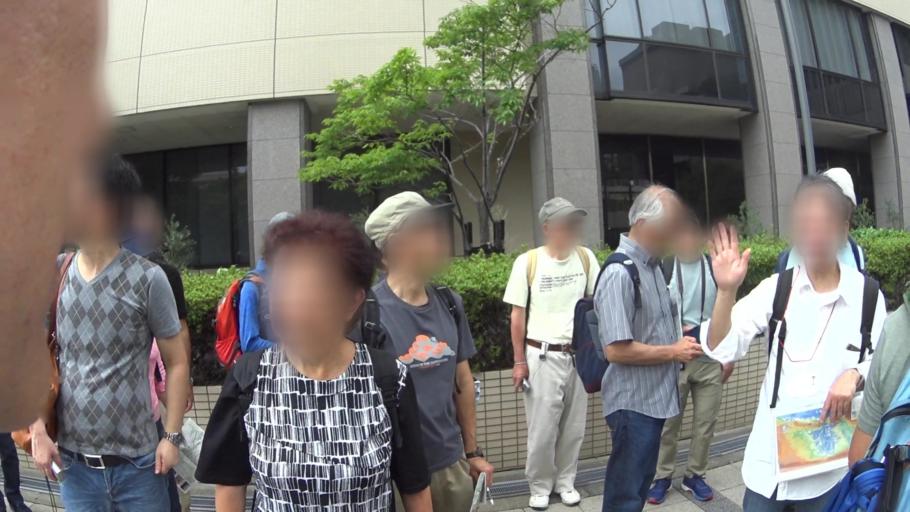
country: JP
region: Osaka
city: Osaka-shi
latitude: 34.7073
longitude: 135.4947
